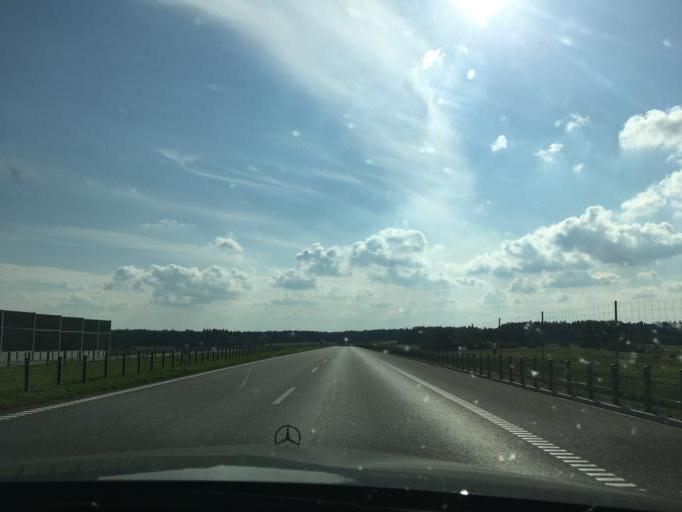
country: PL
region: Podlasie
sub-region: Powiat suwalski
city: Raczki
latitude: 54.0189
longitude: 22.8753
